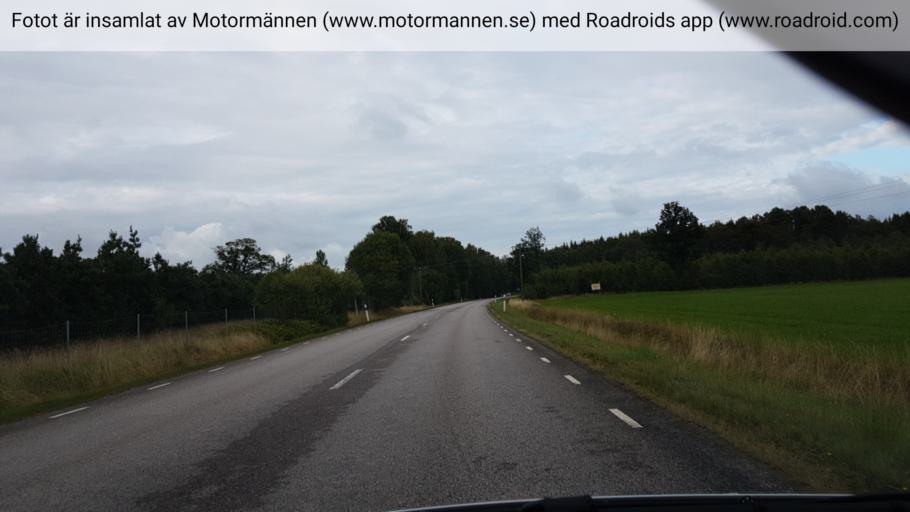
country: SE
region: Vaestra Goetaland
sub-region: Hjo Kommun
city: Hjo
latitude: 58.2512
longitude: 14.2339
